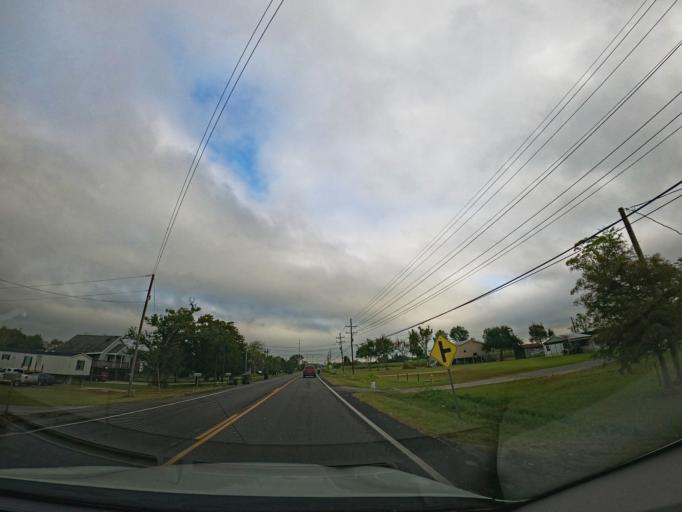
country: US
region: Louisiana
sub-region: Terrebonne Parish
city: Presquille
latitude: 29.5165
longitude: -90.6756
